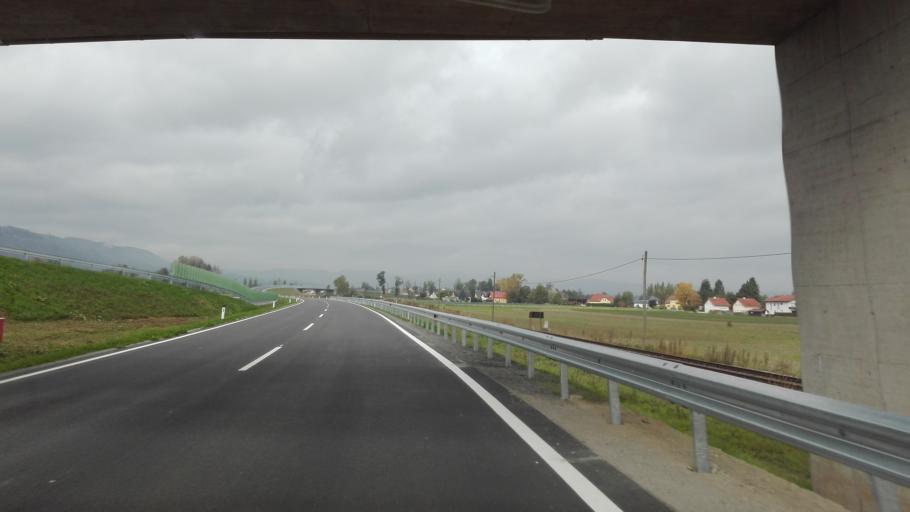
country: AT
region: Upper Austria
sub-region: Politischer Bezirk Urfahr-Umgebung
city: Feldkirchen an der Donau
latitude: 48.3250
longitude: 14.0096
